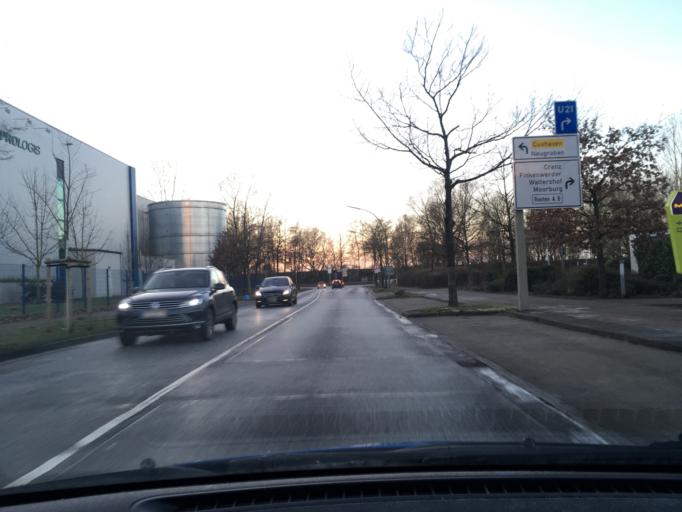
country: DE
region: Hamburg
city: Altona
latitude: 53.4824
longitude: 9.9023
